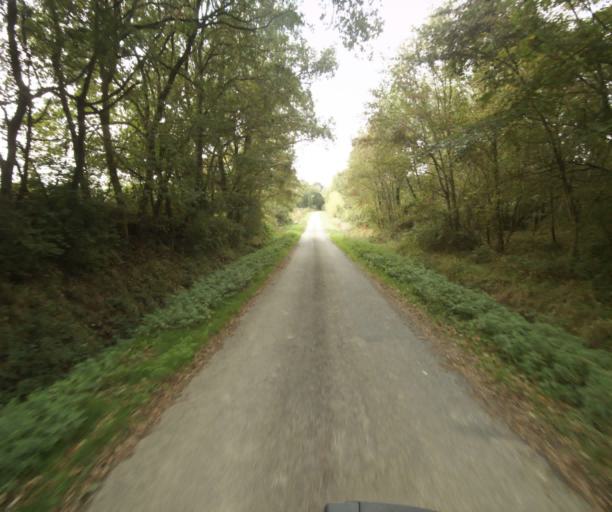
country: FR
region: Midi-Pyrenees
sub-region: Departement du Tarn-et-Garonne
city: Verdun-sur-Garonne
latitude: 43.8484
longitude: 1.1666
